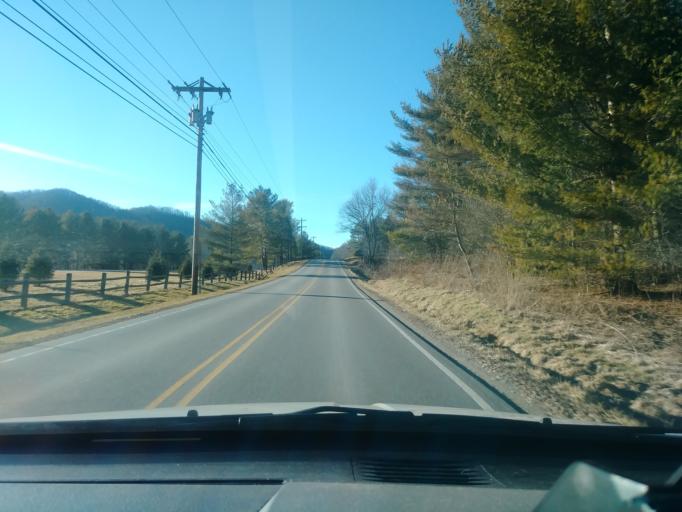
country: US
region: North Carolina
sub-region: Avery County
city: Banner Elk
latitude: 36.1605
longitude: -81.8936
